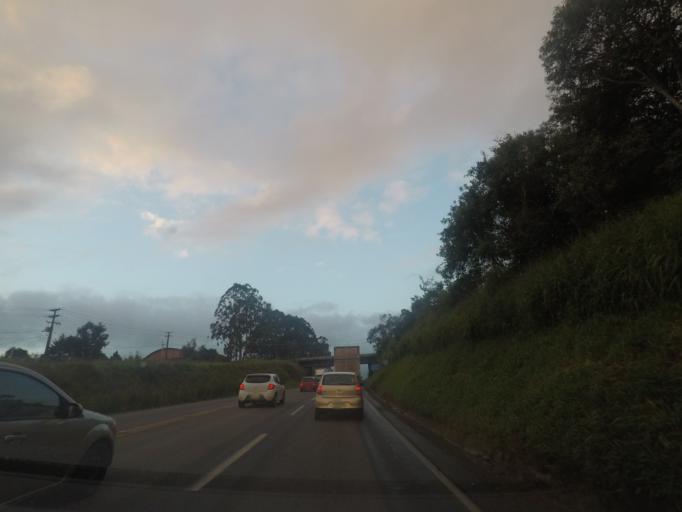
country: BR
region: Parana
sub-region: Curitiba
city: Curitiba
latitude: -25.4089
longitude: -49.3648
